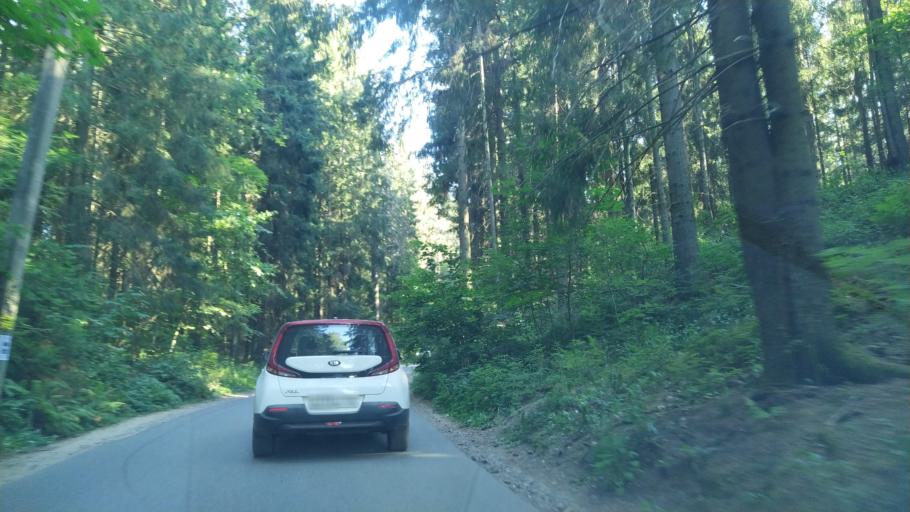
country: RU
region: Leningrad
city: Toksovo
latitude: 60.1706
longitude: 30.5323
